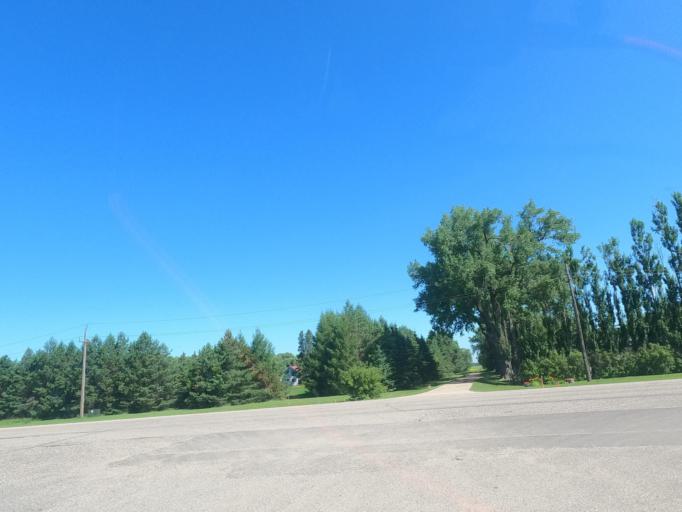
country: CA
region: Manitoba
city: Carberry
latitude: 49.5622
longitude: -99.2909
